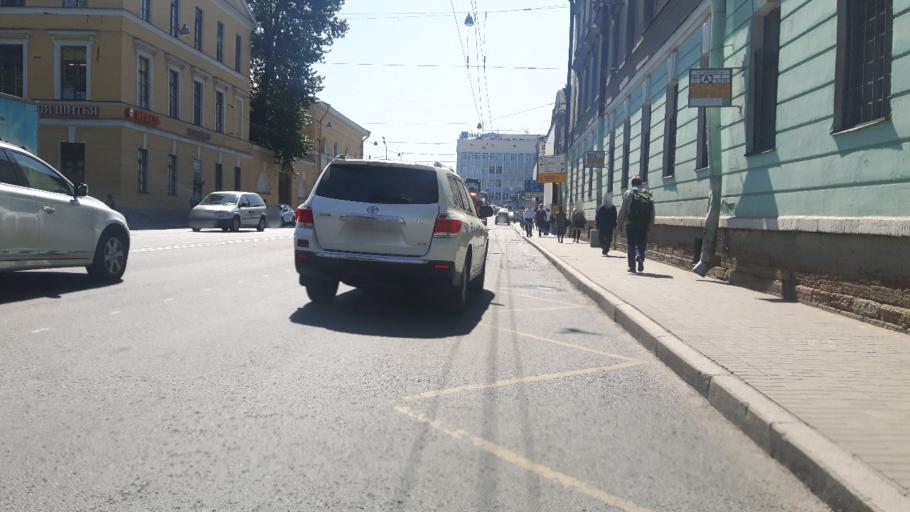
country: RU
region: St.-Petersburg
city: Admiralteisky
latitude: 59.9104
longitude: 30.2976
